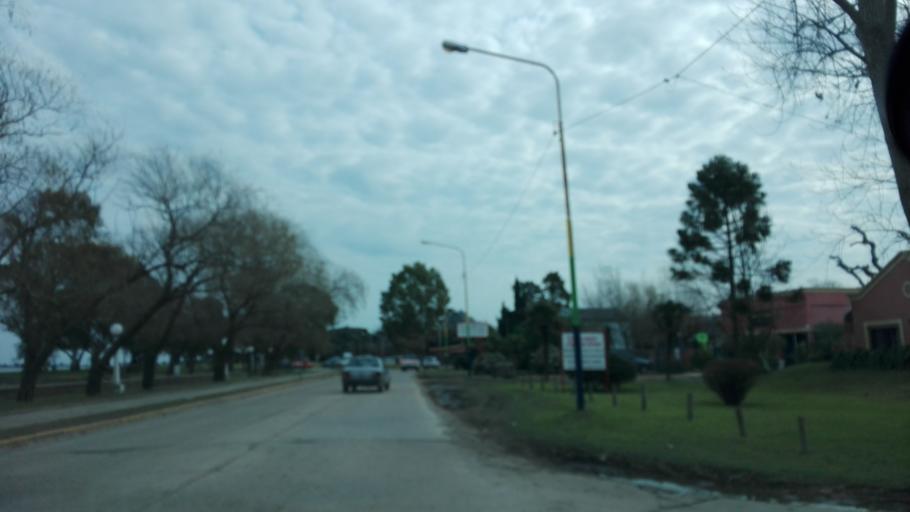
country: AR
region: Buenos Aires
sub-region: Partido de Chascomus
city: Chascomus
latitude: -35.5831
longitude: -58.0034
